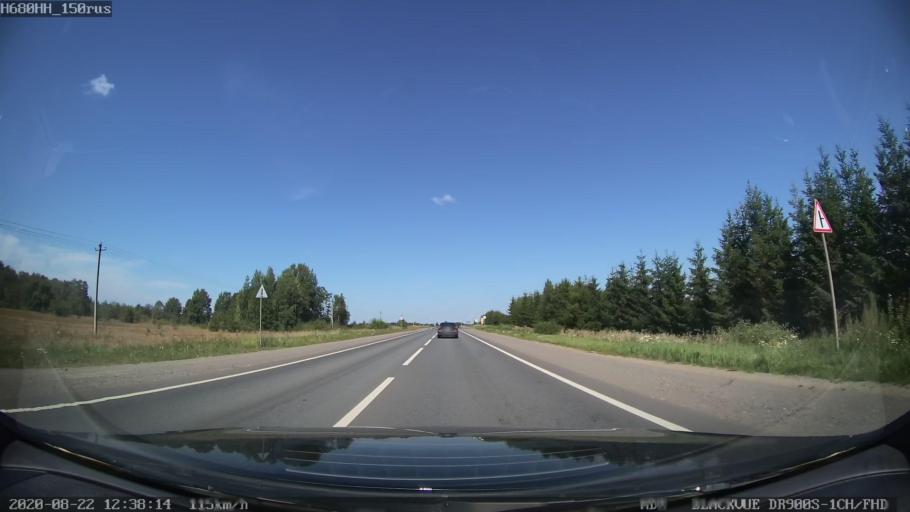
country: RU
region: Tverskaya
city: Rameshki
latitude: 57.3108
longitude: 36.0885
